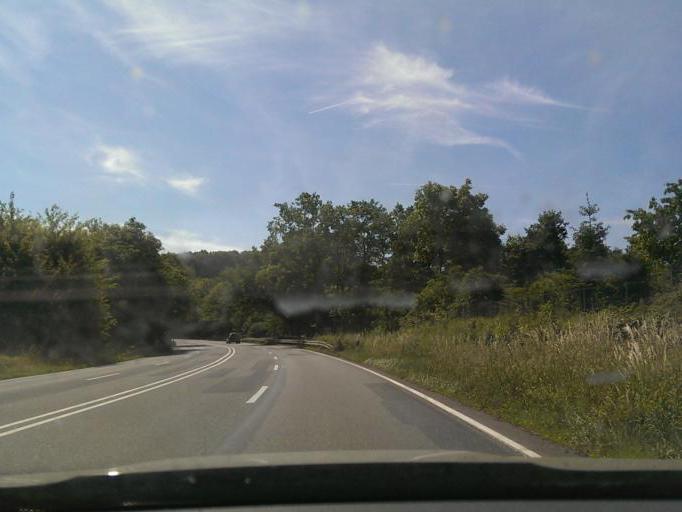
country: DE
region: Lower Saxony
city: Alfeld
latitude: 51.9847
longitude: 9.8041
